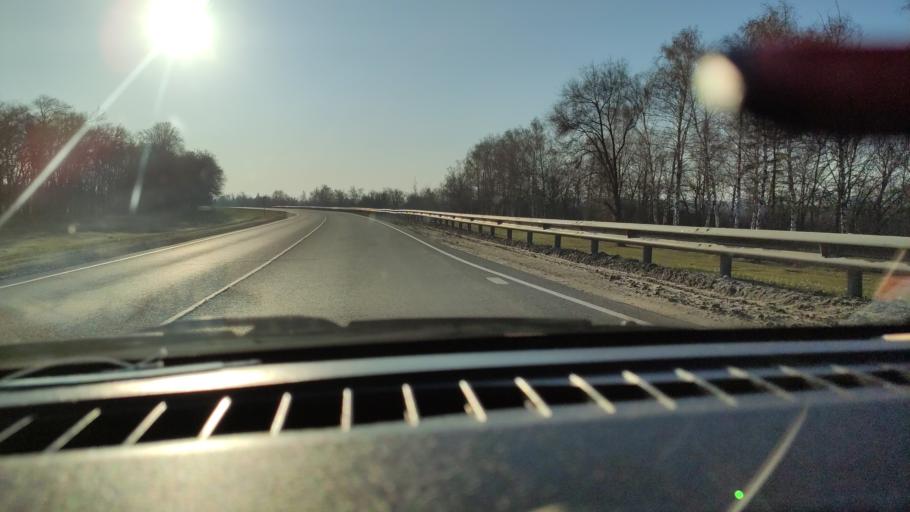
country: RU
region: Saratov
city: Tersa
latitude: 52.0829
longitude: 47.5609
